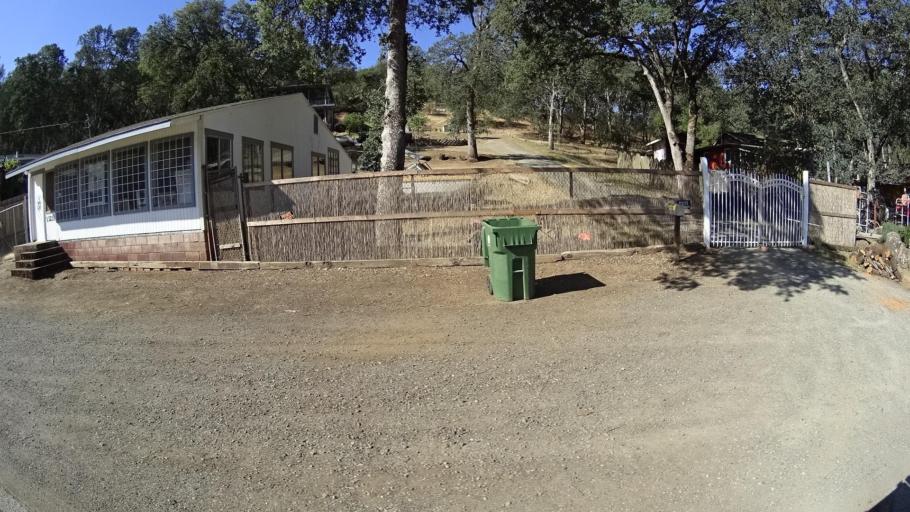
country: US
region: California
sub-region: Lake County
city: Clearlake
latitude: 38.9730
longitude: -122.6647
